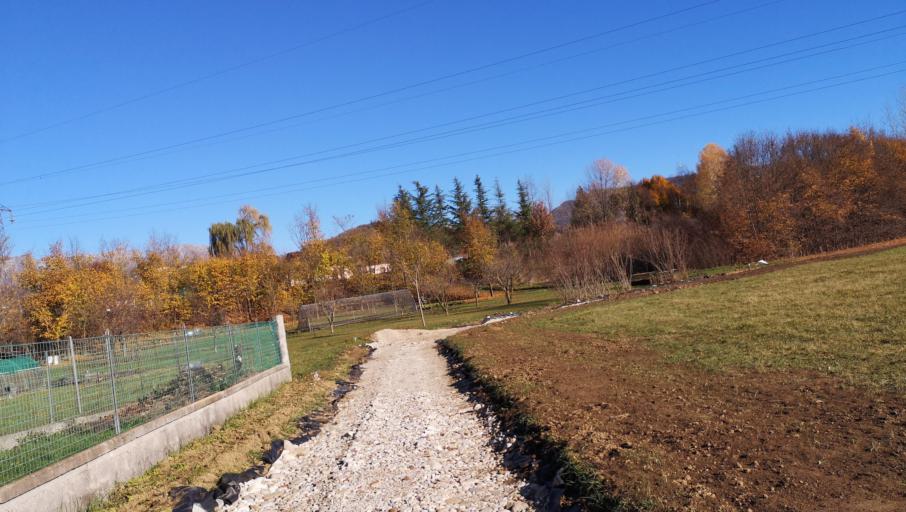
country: IT
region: Friuli Venezia Giulia
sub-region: Provincia di Udine
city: Magnano in Riviera
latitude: 46.2099
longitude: 13.1977
